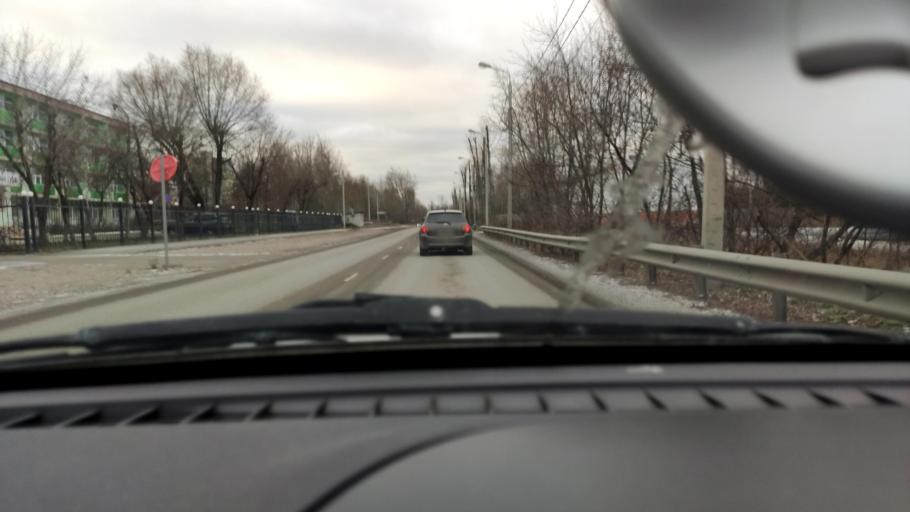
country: RU
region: Perm
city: Kondratovo
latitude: 57.9705
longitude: 56.1278
